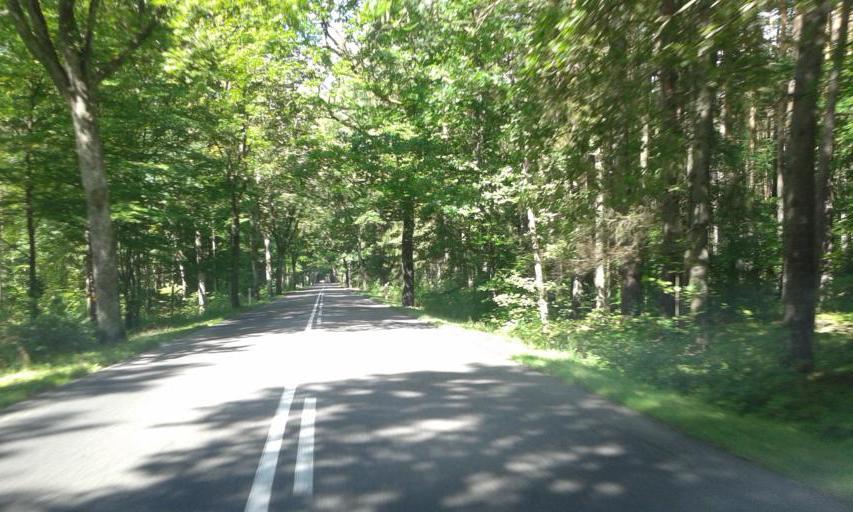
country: PL
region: West Pomeranian Voivodeship
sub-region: Powiat slawienski
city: Slawno
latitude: 54.2462
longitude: 16.7011
